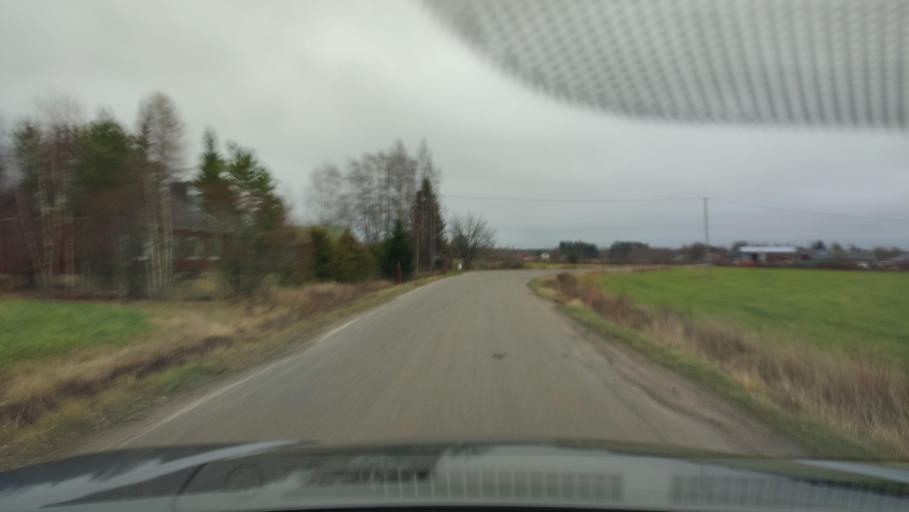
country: FI
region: Southern Ostrobothnia
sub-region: Suupohja
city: Isojoki
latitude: 62.1928
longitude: 21.9541
